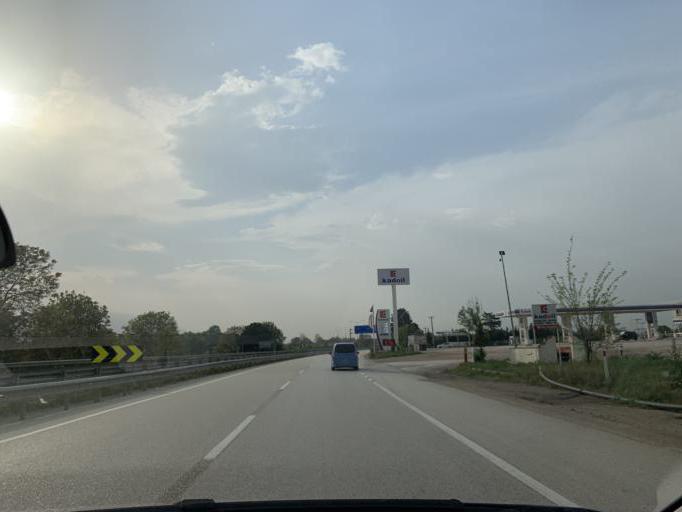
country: TR
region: Bursa
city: Kursunlu
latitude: 40.0393
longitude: 29.5965
